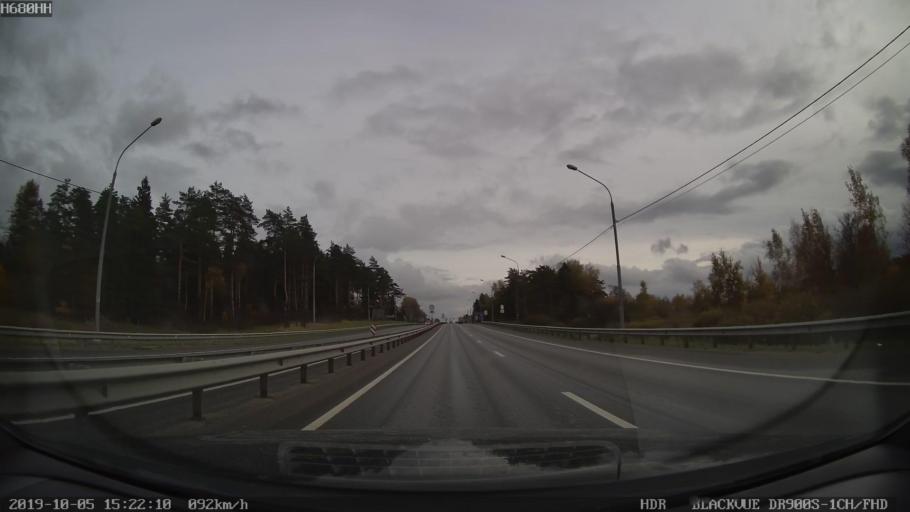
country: RU
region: Moskovskaya
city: Solnechnogorsk
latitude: 56.2222
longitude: 36.9218
